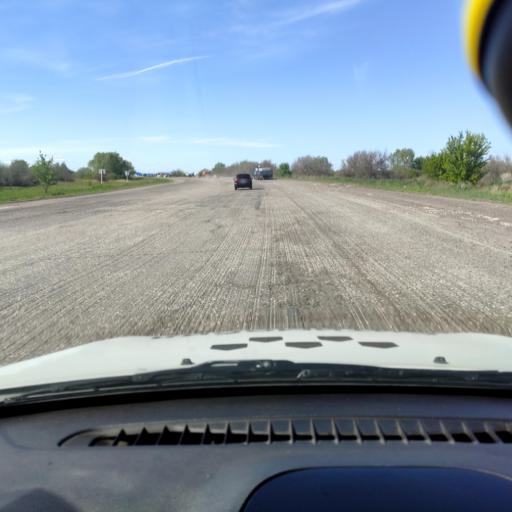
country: RU
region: Samara
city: Tol'yatti
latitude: 53.6606
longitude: 49.4250
